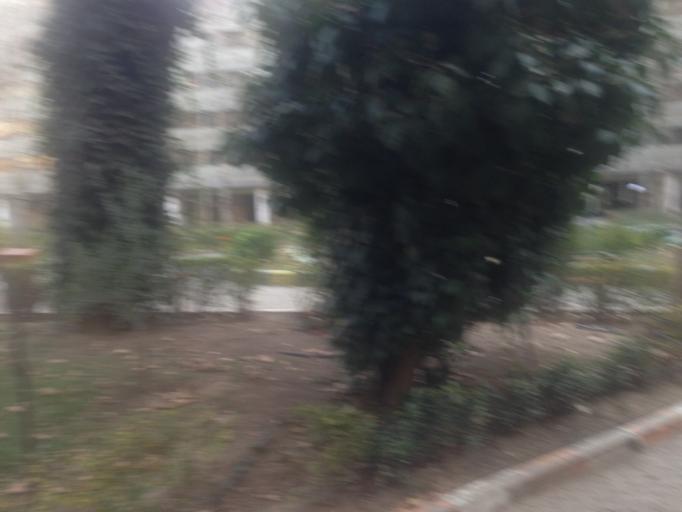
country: IR
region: Tehran
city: Tehran
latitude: 35.7124
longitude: 51.3118
